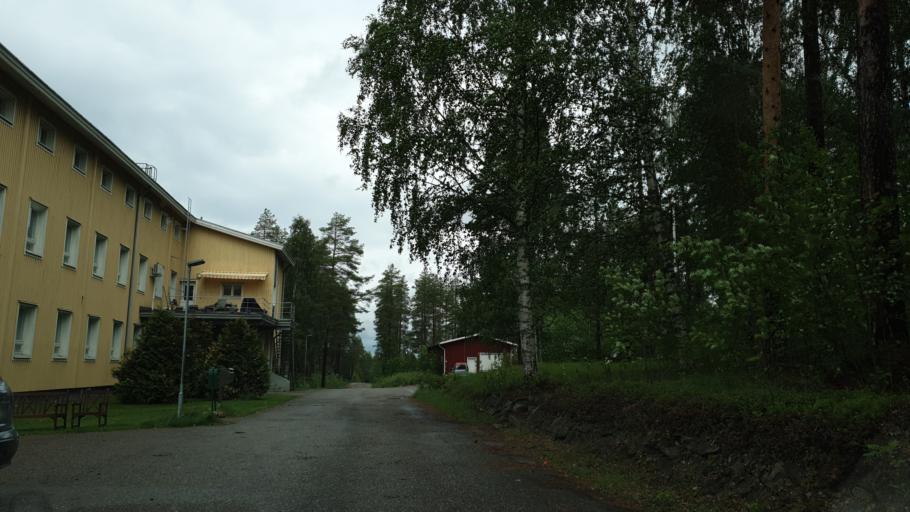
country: FI
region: Kainuu
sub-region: Kehys-Kainuu
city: Kuhmo
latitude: 64.0943
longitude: 29.4343
